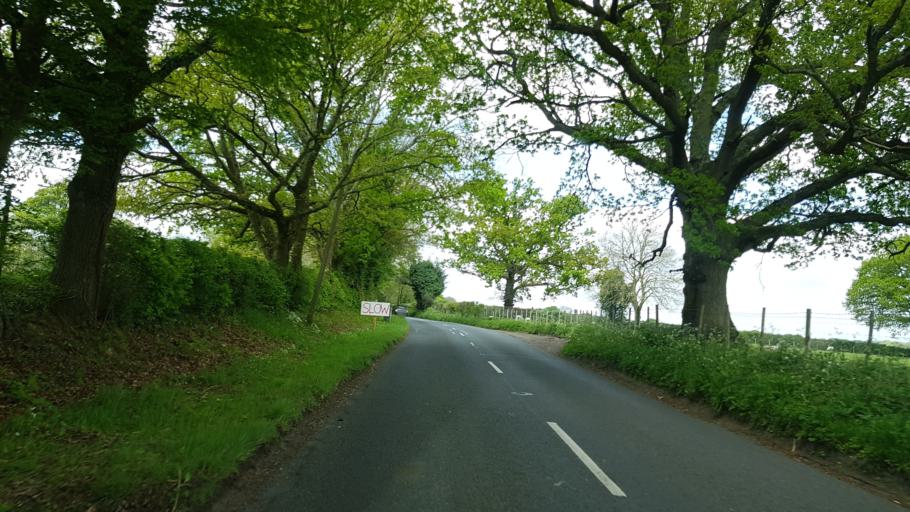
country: GB
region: England
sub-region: East Sussex
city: Robertsbridge
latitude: 51.0344
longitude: 0.4374
